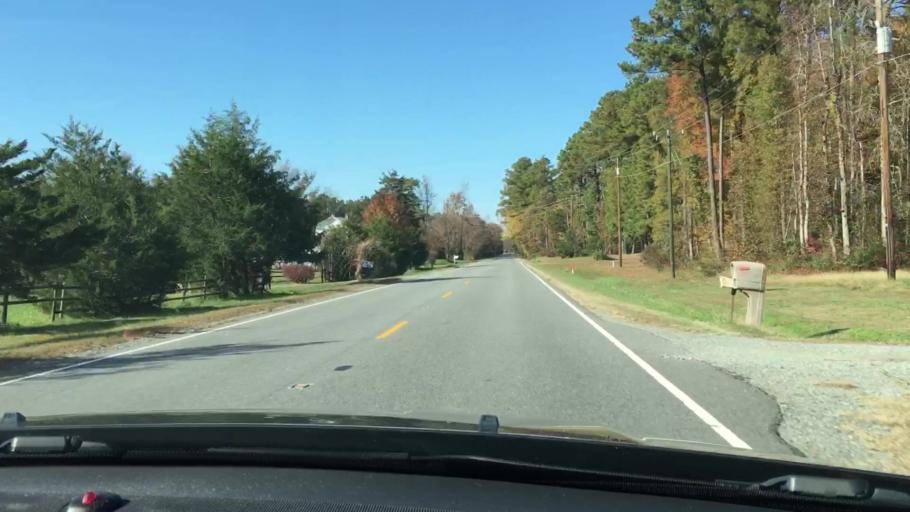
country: US
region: Virginia
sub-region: King William County
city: King William
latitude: 37.6637
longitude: -76.9631
